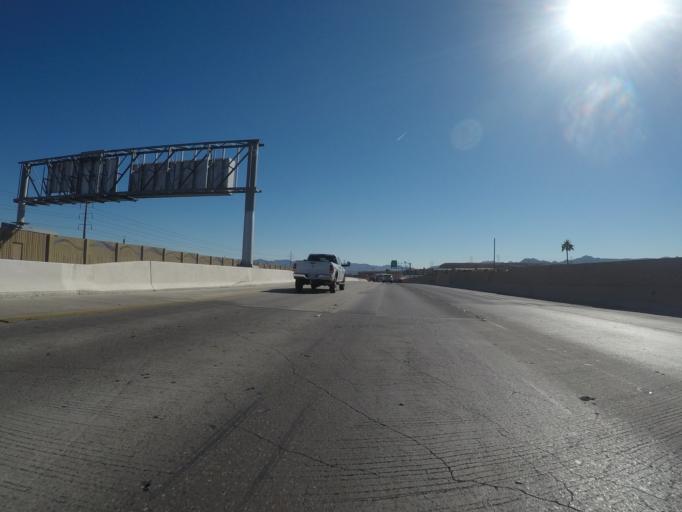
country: US
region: Nevada
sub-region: Clark County
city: Whitney
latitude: 36.0918
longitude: -115.0730
